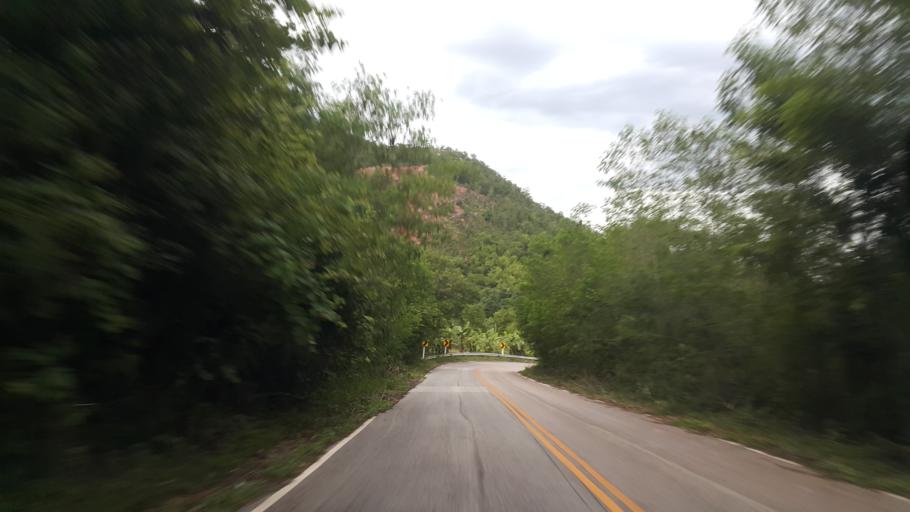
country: TH
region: Loei
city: Na Haeo
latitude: 17.4923
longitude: 101.1774
